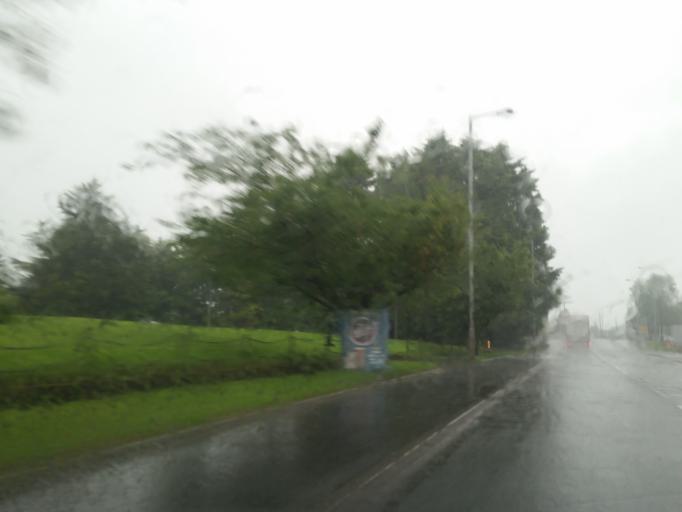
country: GB
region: Northern Ireland
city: Fivemiletown
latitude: 54.4147
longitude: -7.1637
